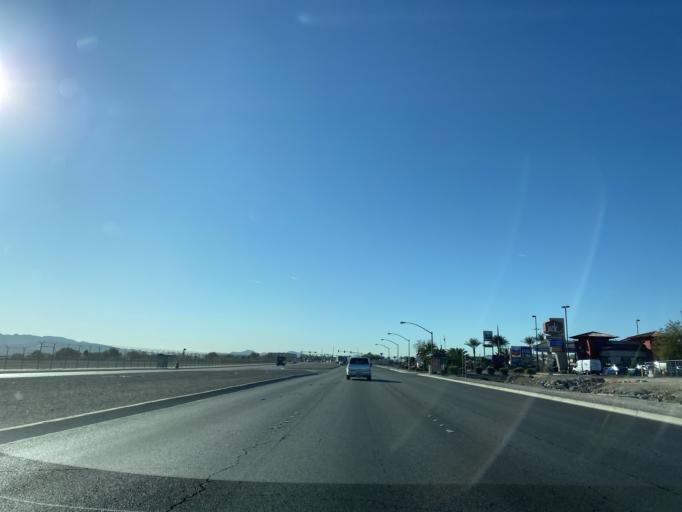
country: US
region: Nevada
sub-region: Clark County
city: Paradise
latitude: 36.0755
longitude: -115.1728
